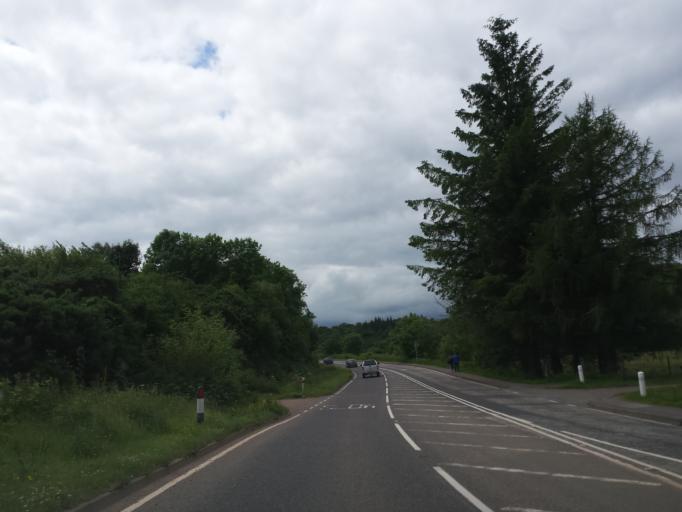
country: GB
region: Scotland
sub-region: Argyll and Bute
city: Oban
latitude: 56.4273
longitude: -5.4620
